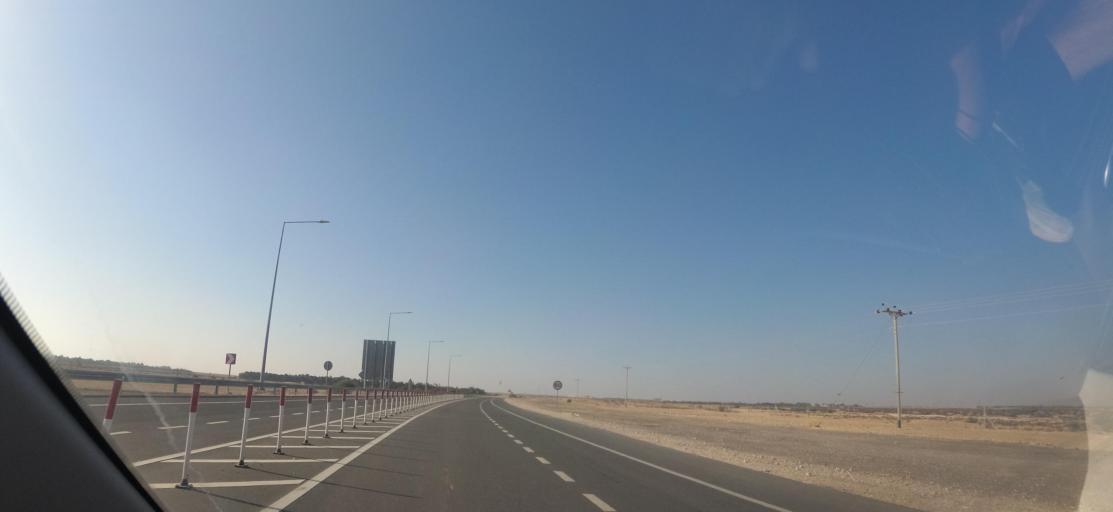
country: QA
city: Al Ghuwayriyah
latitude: 25.8485
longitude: 51.2656
